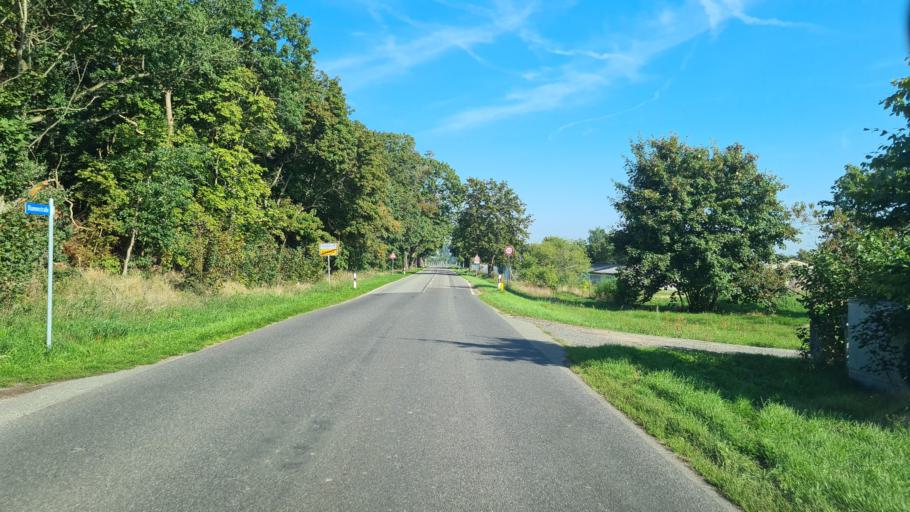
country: DE
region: Brandenburg
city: Pessin
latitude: 52.6947
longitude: 12.6495
